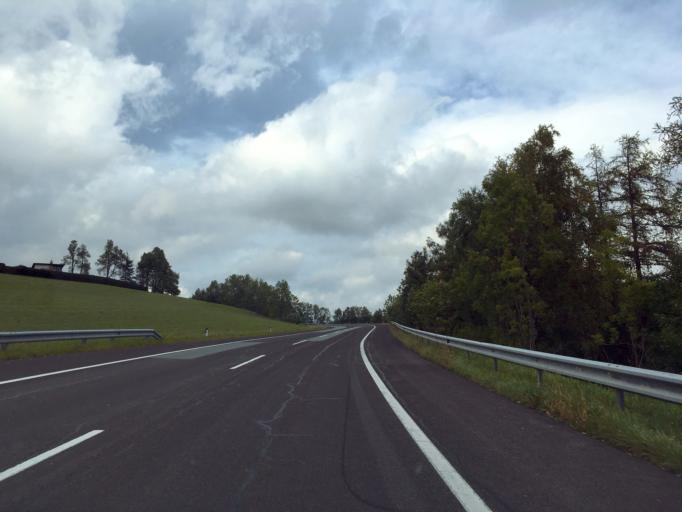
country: AT
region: Lower Austria
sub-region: Politischer Bezirk Neunkirchen
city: Monichkirchen
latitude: 47.4888
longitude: 16.0409
